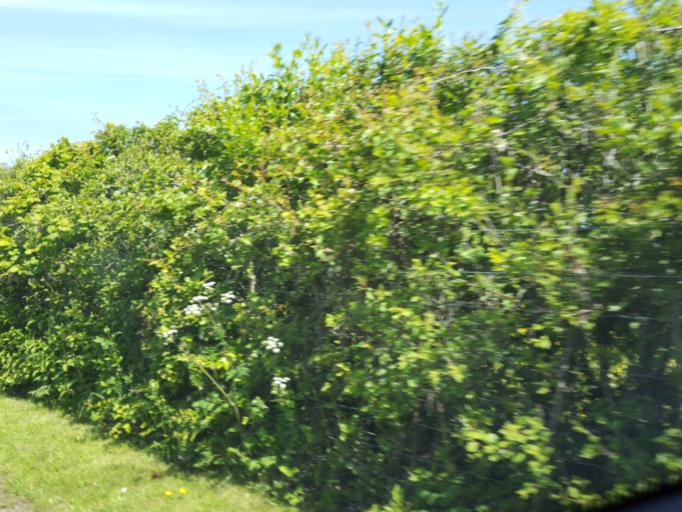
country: GB
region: England
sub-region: Gloucestershire
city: Brimscombe
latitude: 51.7281
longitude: -2.1846
